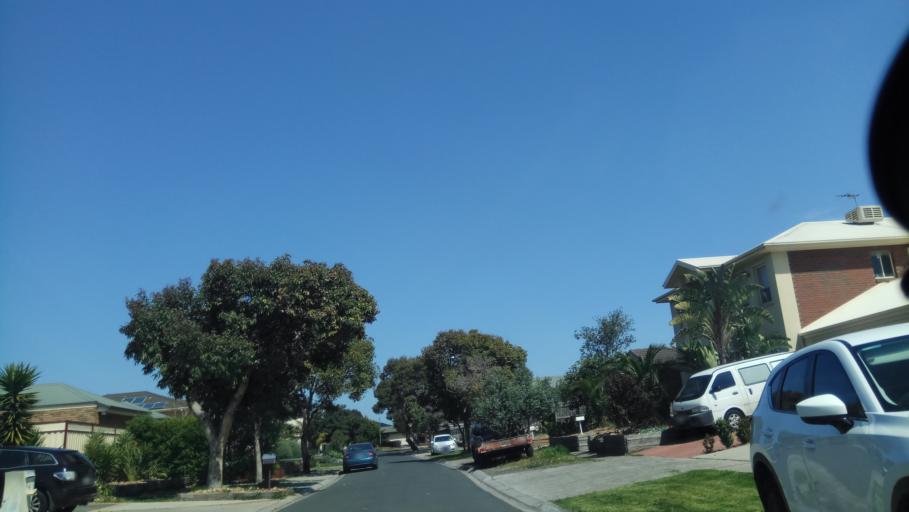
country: AU
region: Victoria
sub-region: Hobsons Bay
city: Altona Meadows
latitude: -37.8849
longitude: 144.7626
